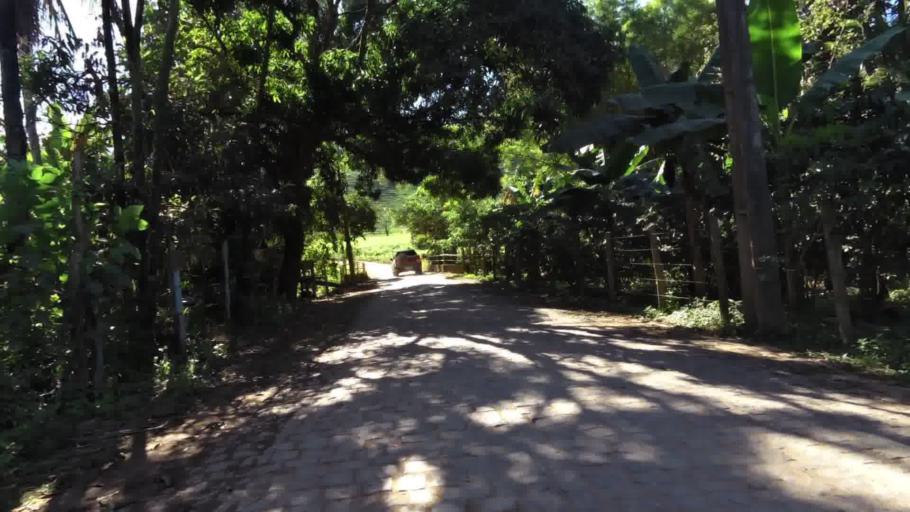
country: BR
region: Espirito Santo
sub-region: Rio Novo Do Sul
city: Rio Novo do Sul
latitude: -20.8530
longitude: -40.9229
